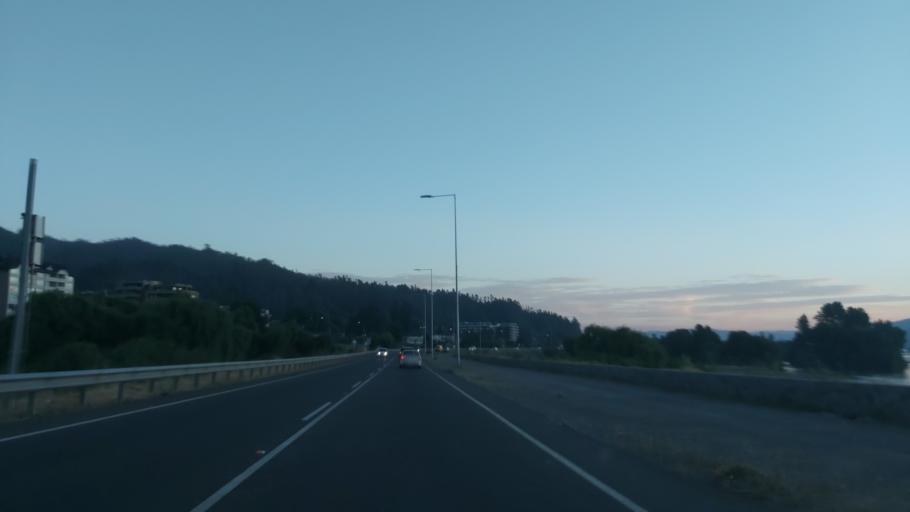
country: CL
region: Biobio
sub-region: Provincia de Concepcion
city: Chiguayante
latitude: -36.8766
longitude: -73.0402
